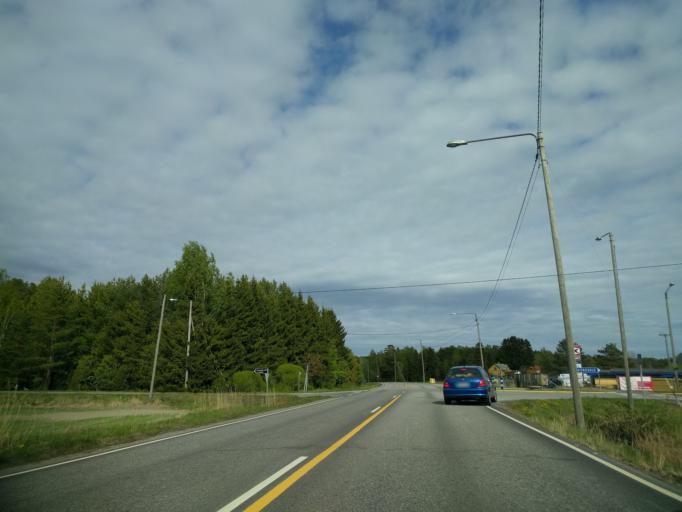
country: FI
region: Varsinais-Suomi
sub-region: Vakka-Suomi
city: Taivassalo
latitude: 60.5647
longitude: 21.6137
